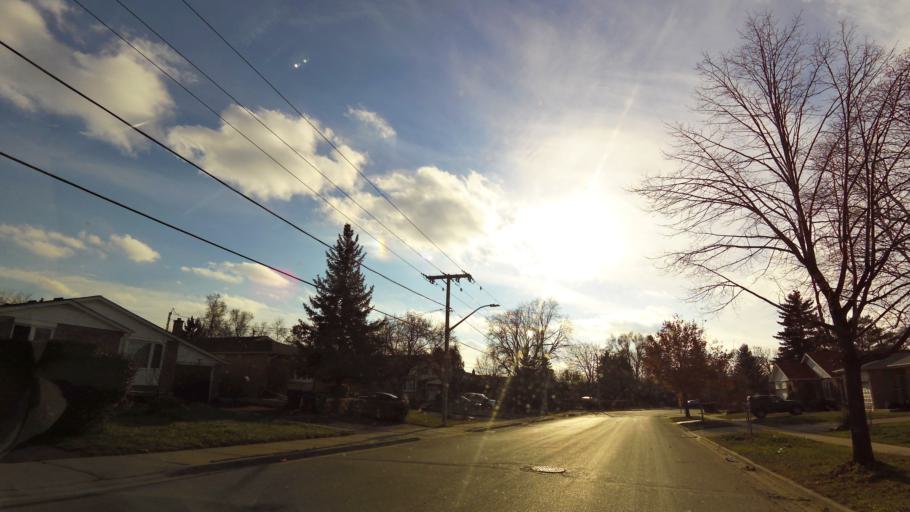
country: CA
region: Ontario
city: Mississauga
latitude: 43.5638
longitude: -79.6679
